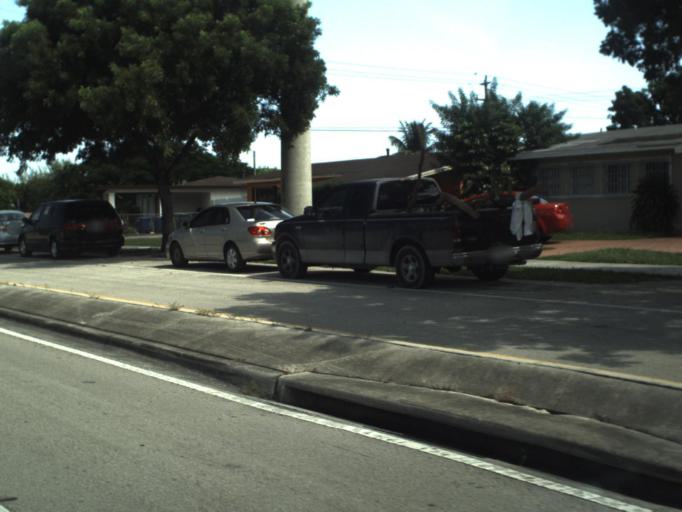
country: US
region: Florida
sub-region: Miami-Dade County
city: Carol City
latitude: 25.9399
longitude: -80.2703
